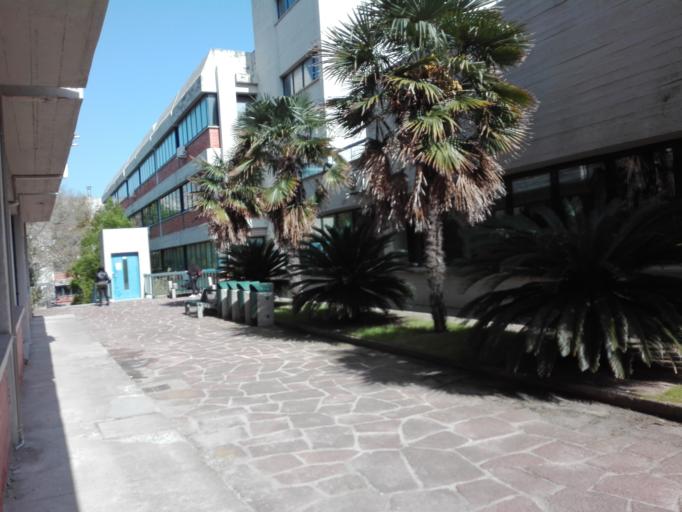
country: IT
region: Sardinia
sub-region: Provincia di Sassari
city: Sassari
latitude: 40.7173
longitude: 8.5539
